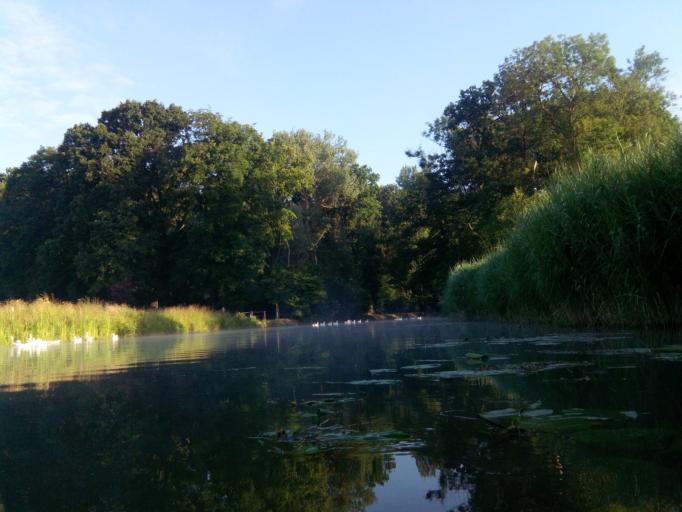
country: NL
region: Utrecht
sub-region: Gemeente Utrecht
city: Lunetten
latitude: 52.0686
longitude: 5.1570
